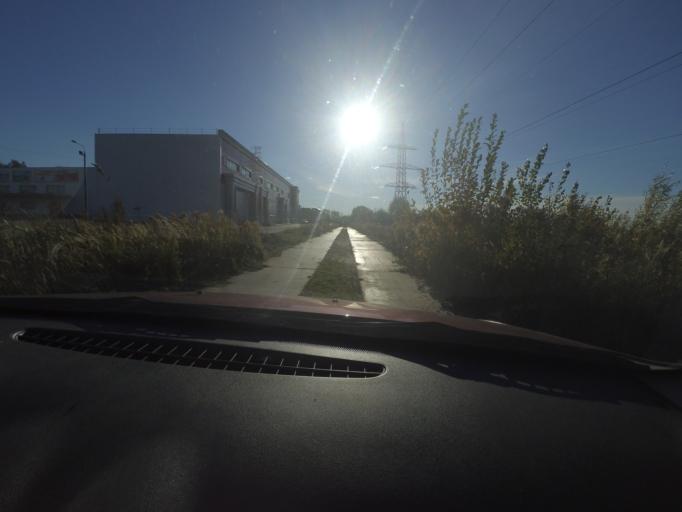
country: RU
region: Nizjnij Novgorod
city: Bor
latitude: 56.3111
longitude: 44.0658
